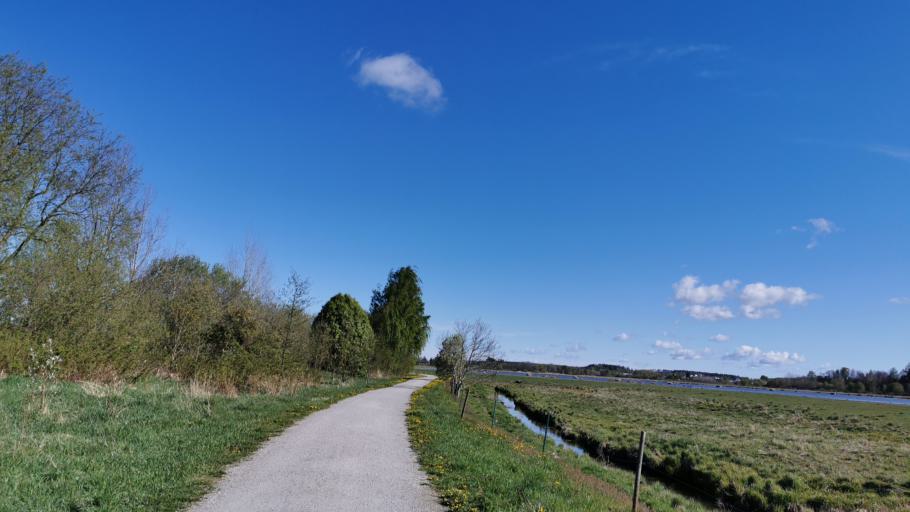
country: SE
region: OErebro
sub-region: Orebro Kommun
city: Orebro
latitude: 59.2969
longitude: 15.2135
